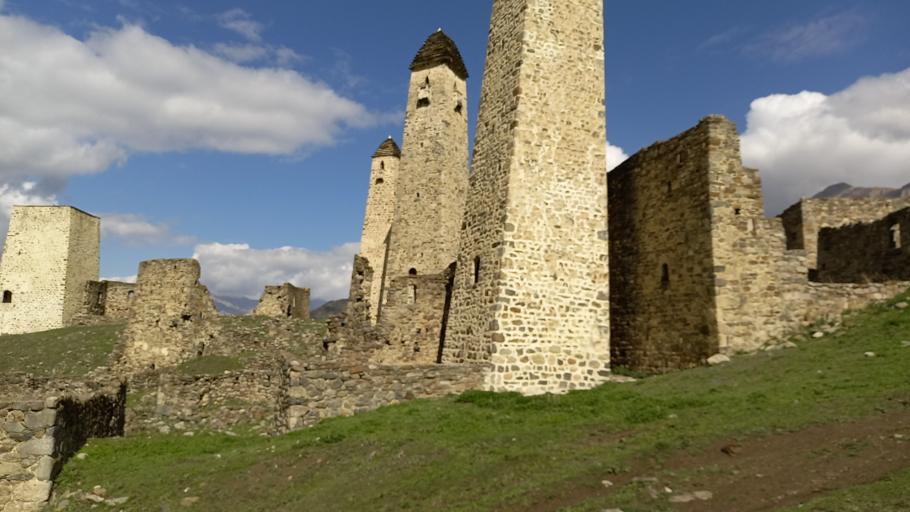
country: RU
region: Ingushetiya
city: Dzhayrakh
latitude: 42.8036
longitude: 44.7604
